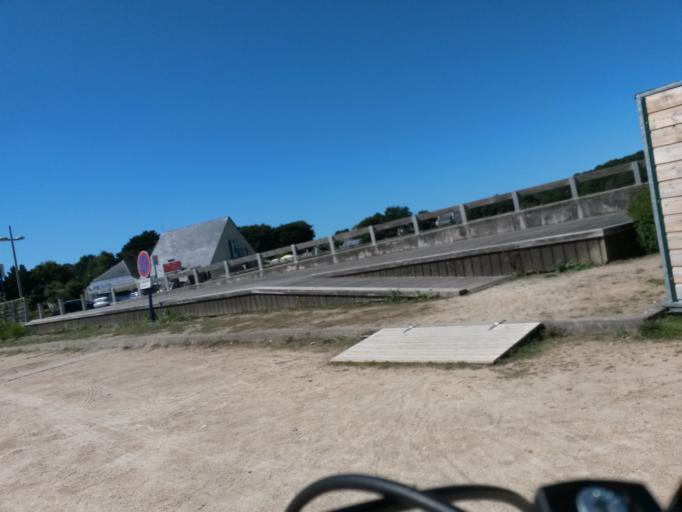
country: FR
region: Pays de la Loire
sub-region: Departement de la Loire-Atlantique
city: Mesquer
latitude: 47.4098
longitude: -2.4646
